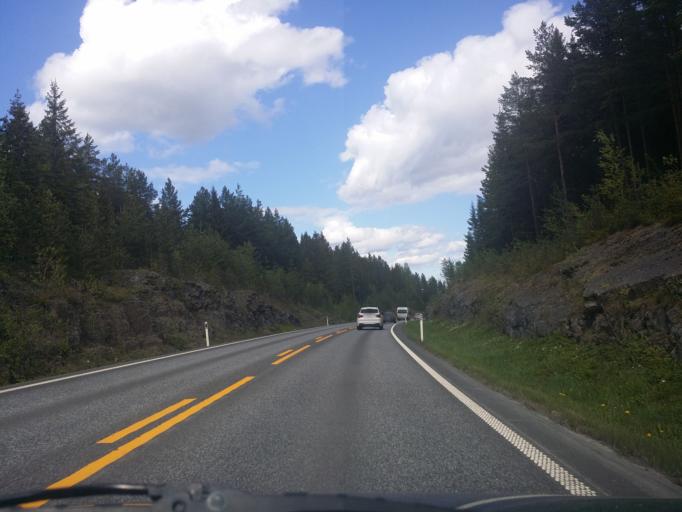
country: NO
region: Oppland
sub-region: Lunner
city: Roa
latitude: 60.2764
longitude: 10.5118
